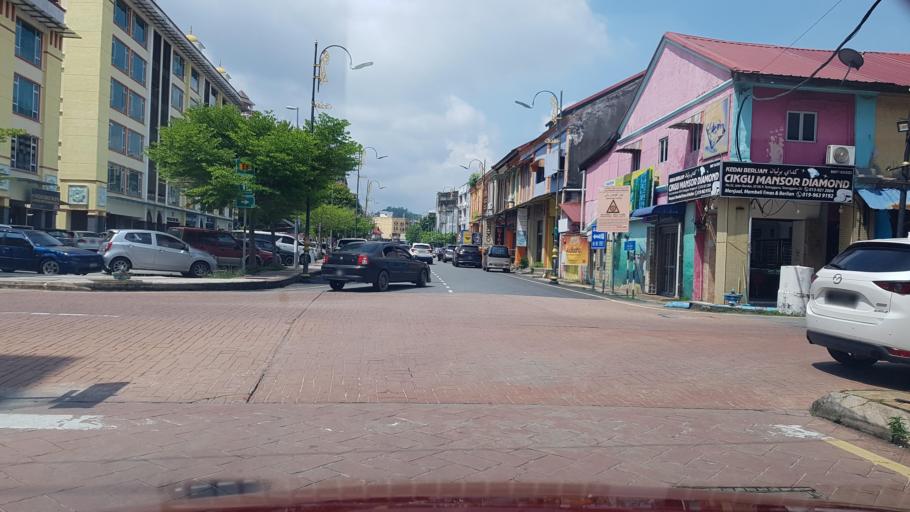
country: MY
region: Terengganu
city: Kuala Terengganu
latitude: 5.3351
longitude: 103.1350
